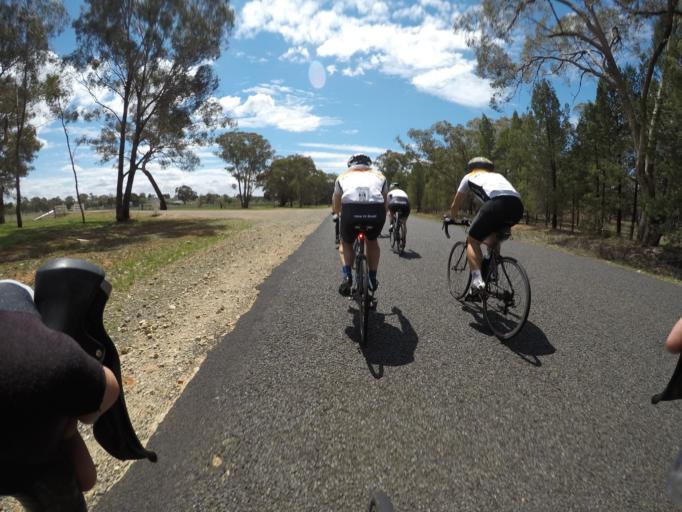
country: AU
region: New South Wales
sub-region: Dubbo Municipality
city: Dubbo
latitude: -32.3523
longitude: 148.5933
